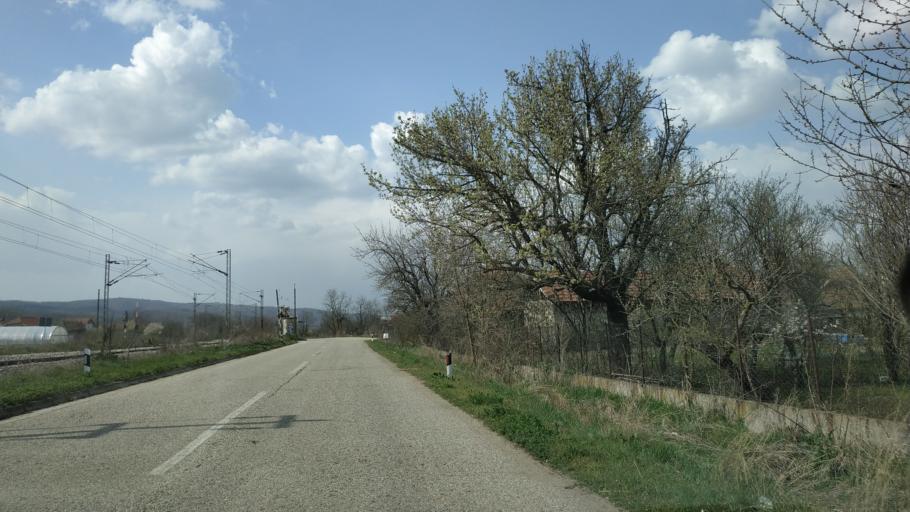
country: RS
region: Central Serbia
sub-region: Nisavski Okrug
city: Razanj
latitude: 43.5720
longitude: 21.5843
